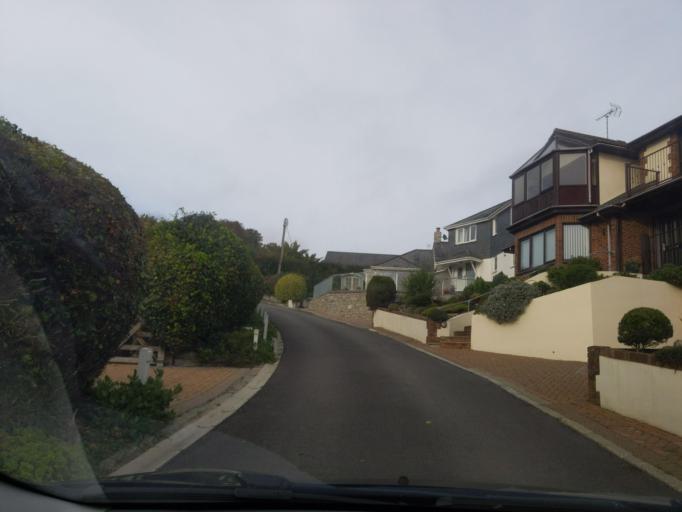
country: GB
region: England
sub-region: Cornwall
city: Looe
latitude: 50.3606
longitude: -4.4394
